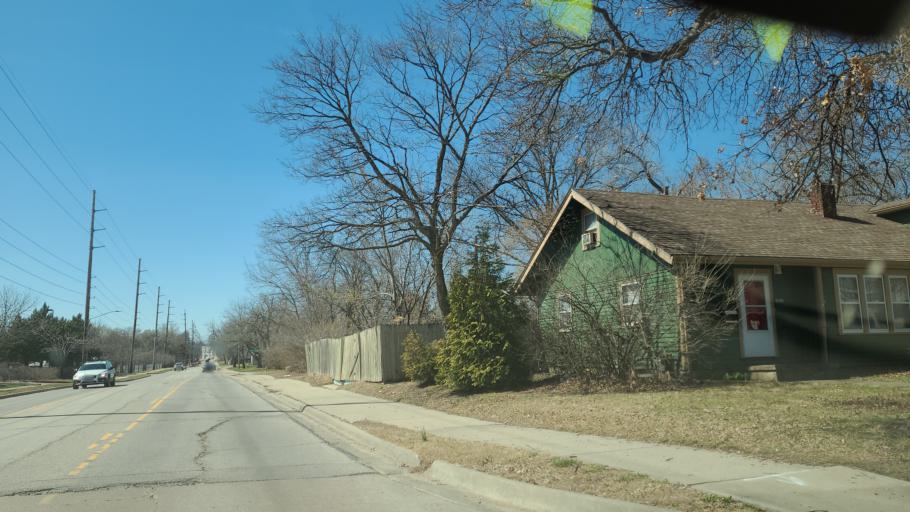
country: US
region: Kansas
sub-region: Douglas County
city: Lawrence
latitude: 38.9502
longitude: -95.2430
